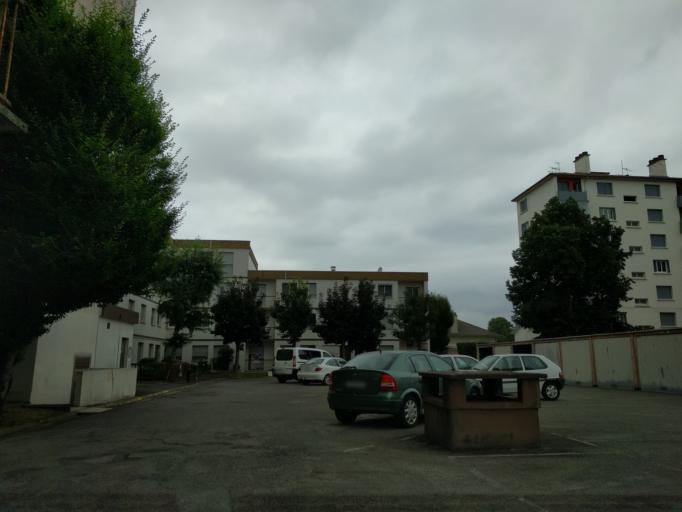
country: FR
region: Midi-Pyrenees
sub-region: Departement des Hautes-Pyrenees
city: Tarbes
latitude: 43.2259
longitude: 0.0660
